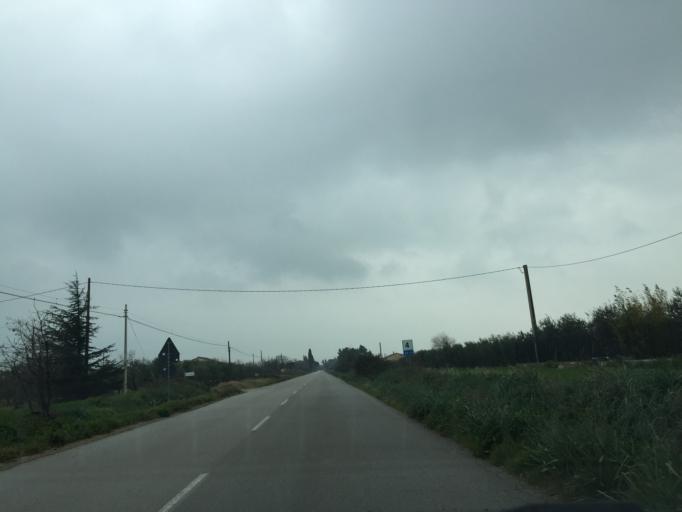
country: IT
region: Apulia
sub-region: Provincia di Foggia
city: Foggia
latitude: 41.4172
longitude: 15.4588
